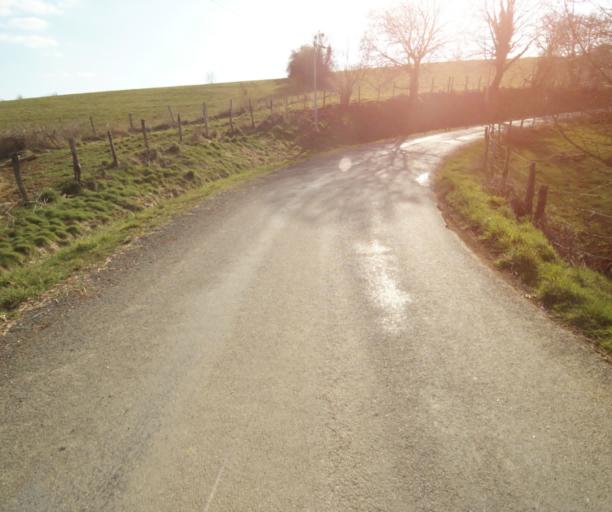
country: FR
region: Limousin
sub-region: Departement de la Correze
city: Saint-Mexant
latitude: 45.3411
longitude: 1.6158
